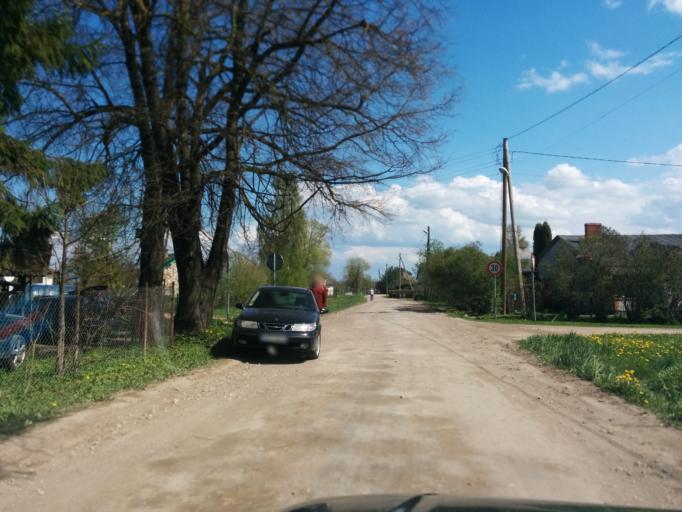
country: LV
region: Jelgava
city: Jelgava
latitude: 56.6301
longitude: 23.7129
